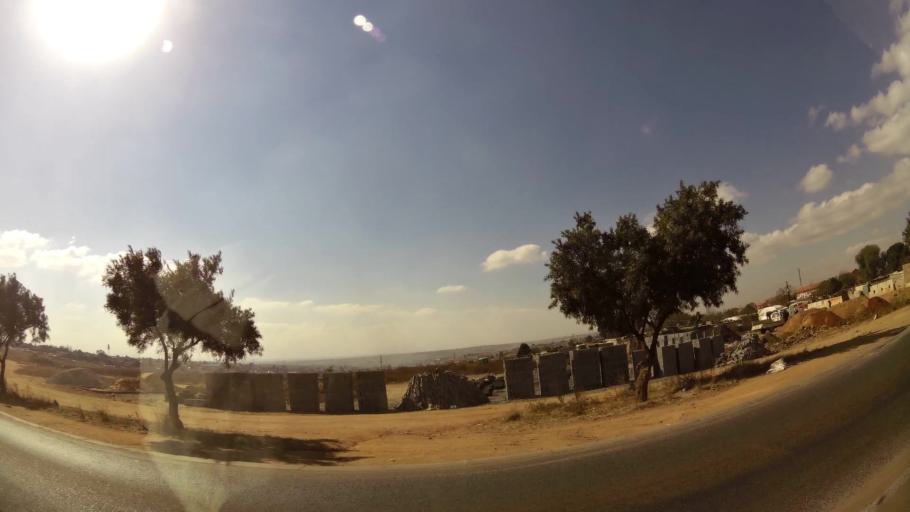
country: ZA
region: Gauteng
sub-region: City of Johannesburg Metropolitan Municipality
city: Midrand
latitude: -26.0276
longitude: 28.1709
